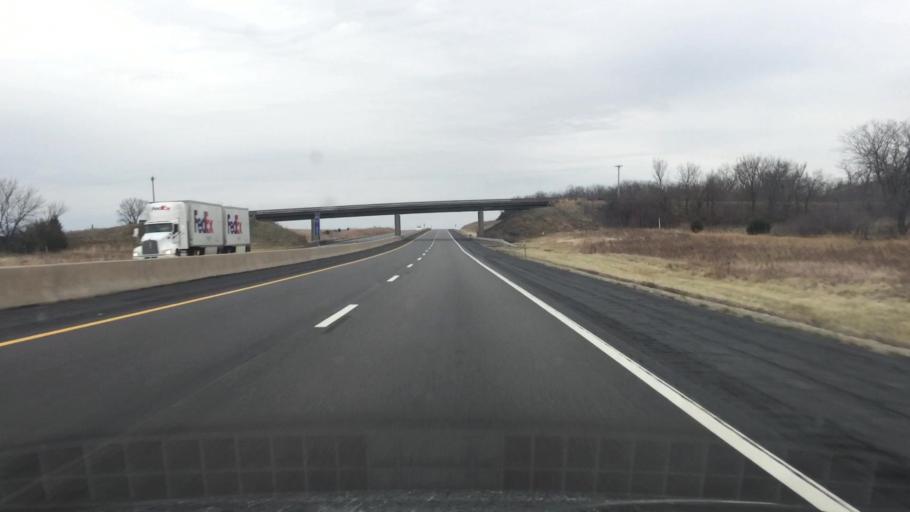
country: US
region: Kansas
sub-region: Shawnee County
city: Auburn
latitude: 38.8132
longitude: -95.8979
